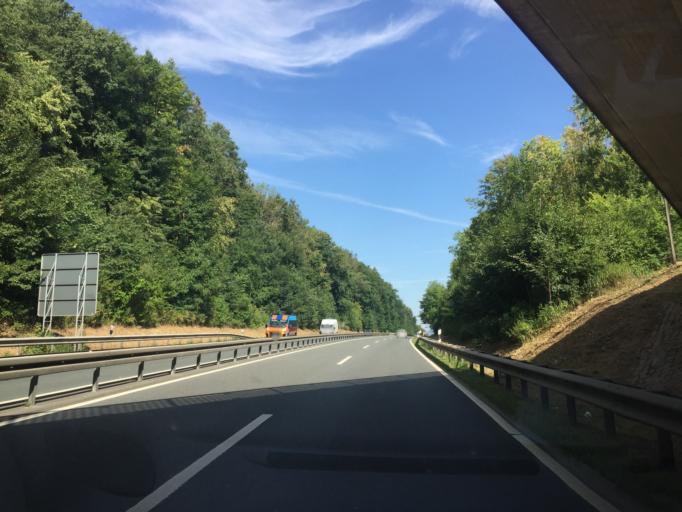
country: DE
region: Lower Saxony
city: Gittelde
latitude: 51.8333
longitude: 10.1865
